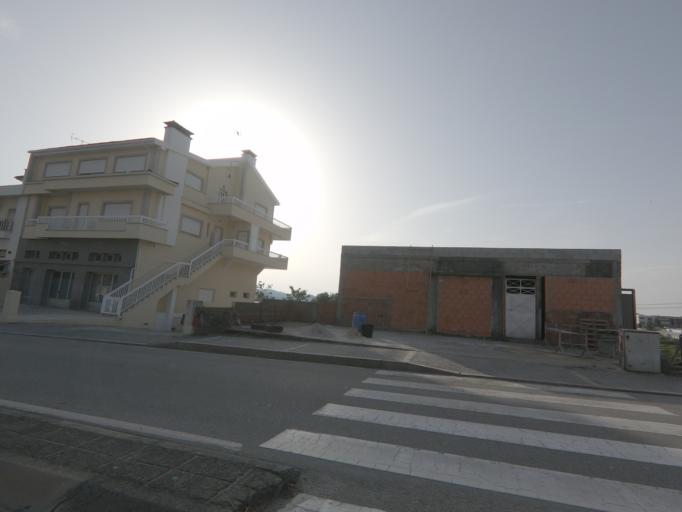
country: PT
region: Vila Real
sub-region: Sabrosa
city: Sabrosa
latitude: 41.2721
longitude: -7.4773
